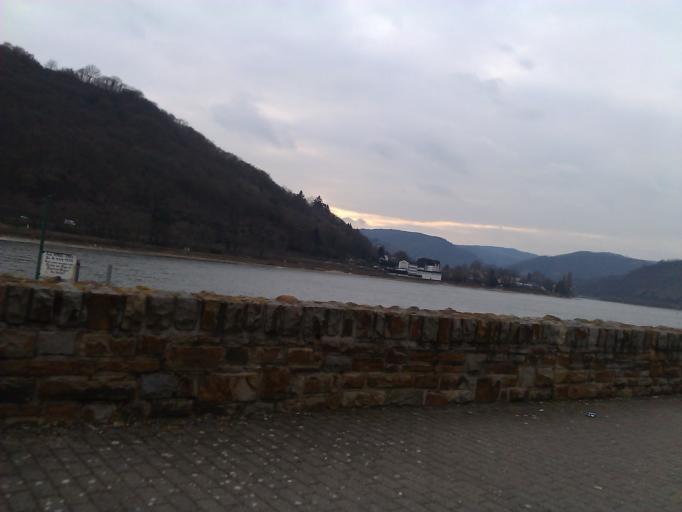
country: DE
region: Rheinland-Pfalz
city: Kamp-Bornhofen
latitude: 50.2269
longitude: 7.6169
